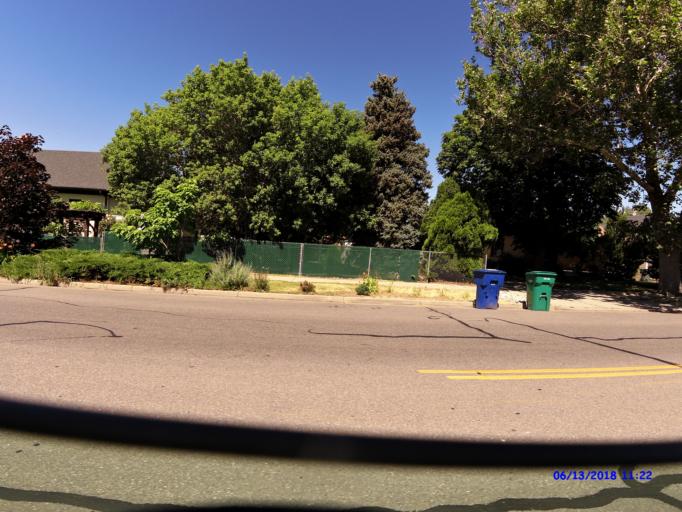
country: US
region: Utah
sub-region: Weber County
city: Ogden
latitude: 41.2293
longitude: -111.9591
